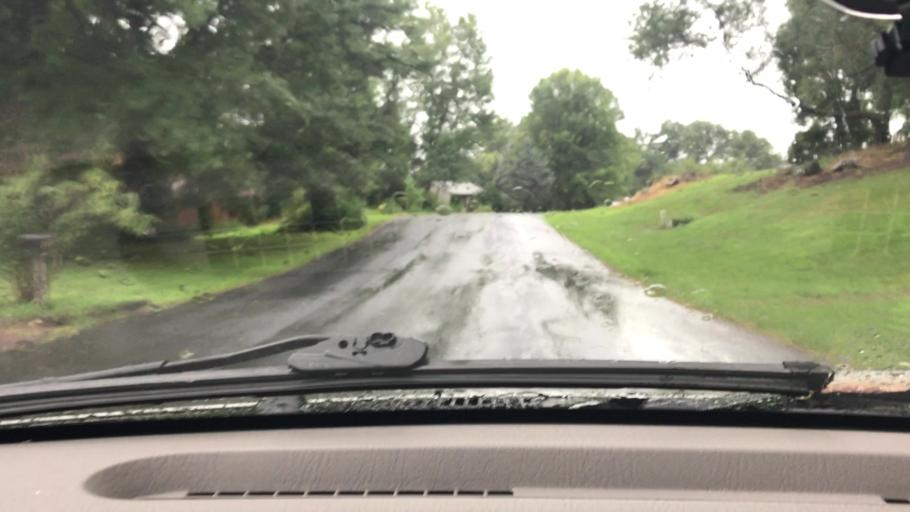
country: US
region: Pennsylvania
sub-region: Lancaster County
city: Bainbridge
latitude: 40.1426
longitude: -76.6579
